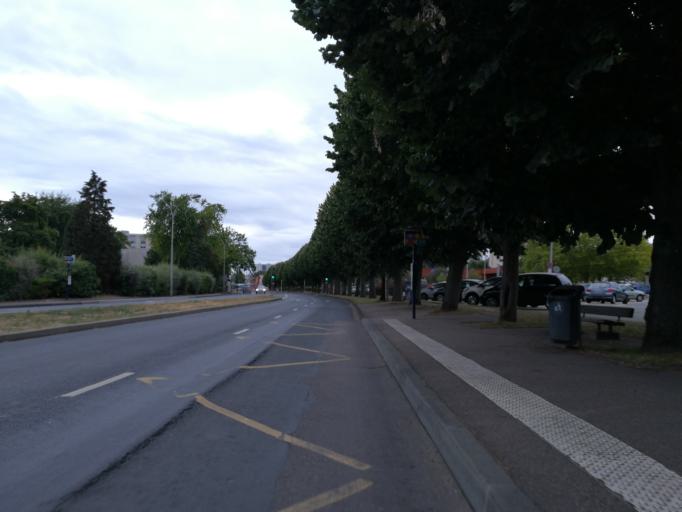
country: FR
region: Haute-Normandie
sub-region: Departement de la Seine-Maritime
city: Mont-Saint-Aignan
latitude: 49.4615
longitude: 1.0813
